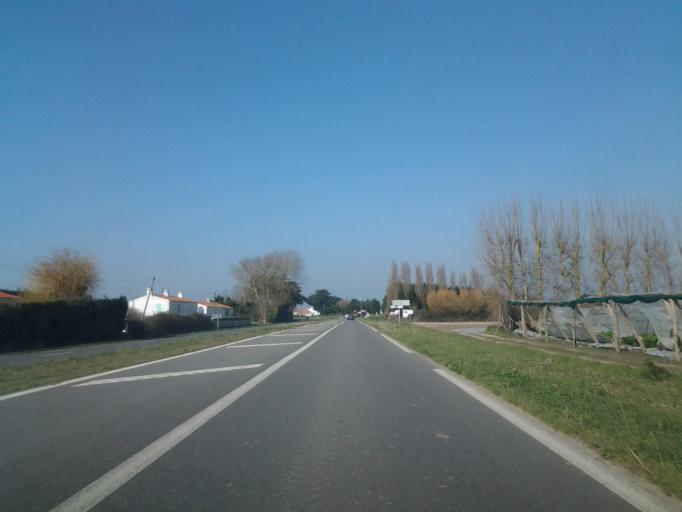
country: FR
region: Pays de la Loire
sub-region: Departement de la Vendee
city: La Gueriniere
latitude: 46.9653
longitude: -2.2120
